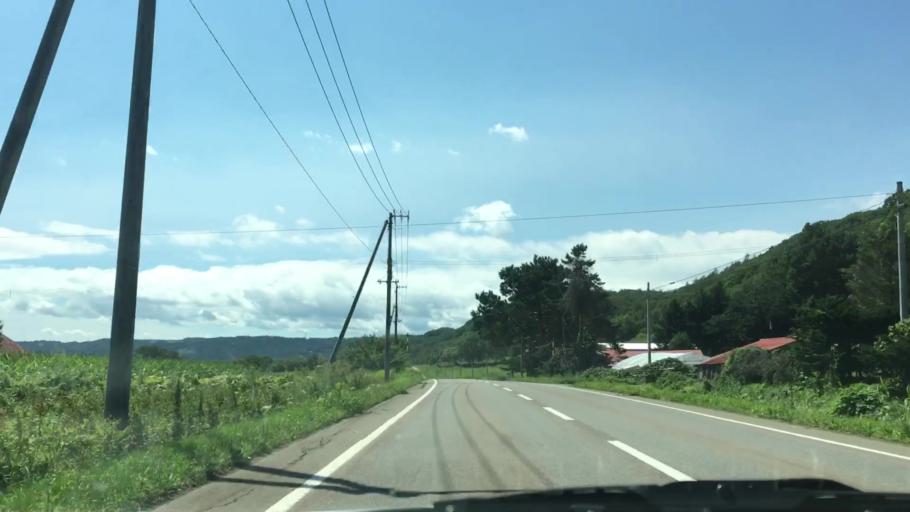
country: JP
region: Hokkaido
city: Otofuke
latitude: 43.2619
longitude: 143.5769
